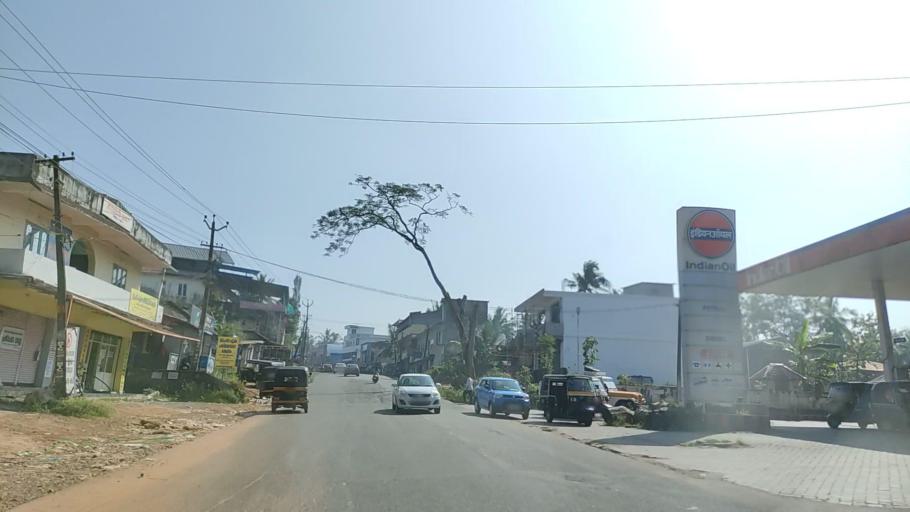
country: IN
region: Kerala
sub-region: Kollam
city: Punalur
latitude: 8.9296
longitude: 76.9294
